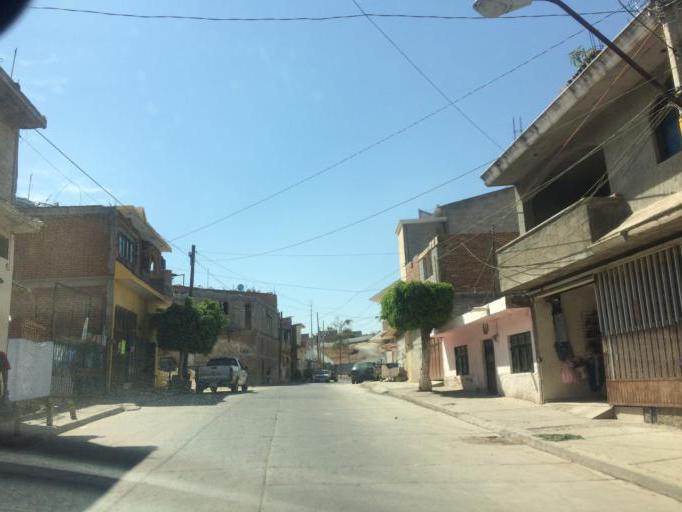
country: MX
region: Guanajuato
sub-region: Leon
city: La Ermita
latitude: 21.1379
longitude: -101.7179
